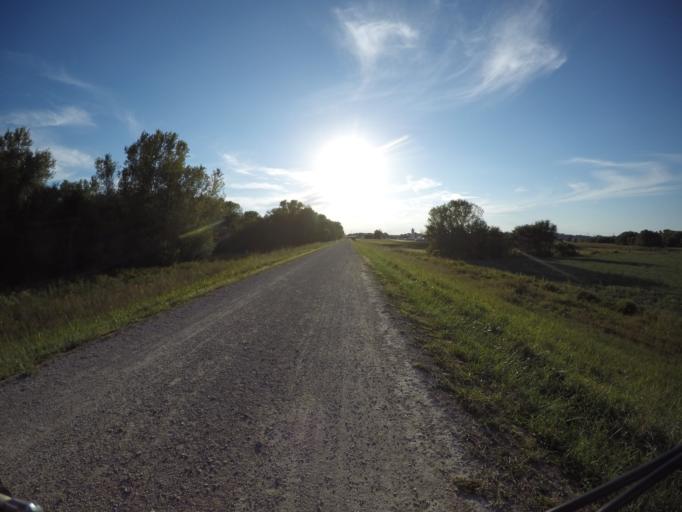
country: US
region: Kansas
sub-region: Riley County
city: Manhattan
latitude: 39.1858
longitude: -96.5345
